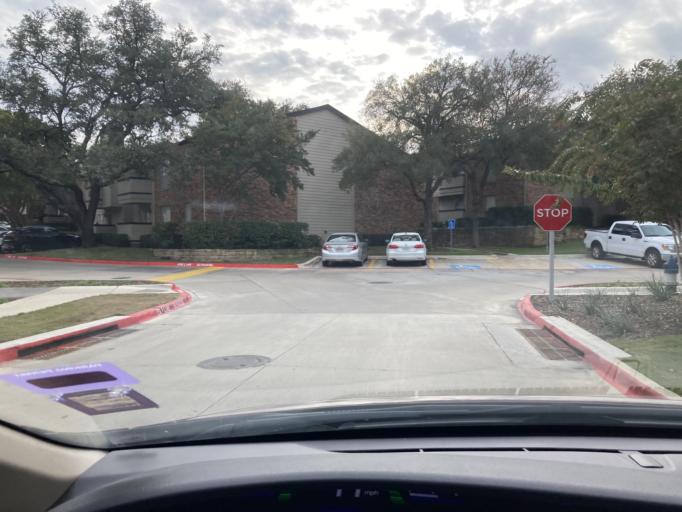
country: US
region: Texas
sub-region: Dallas County
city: University Park
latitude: 32.8581
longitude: -96.7641
